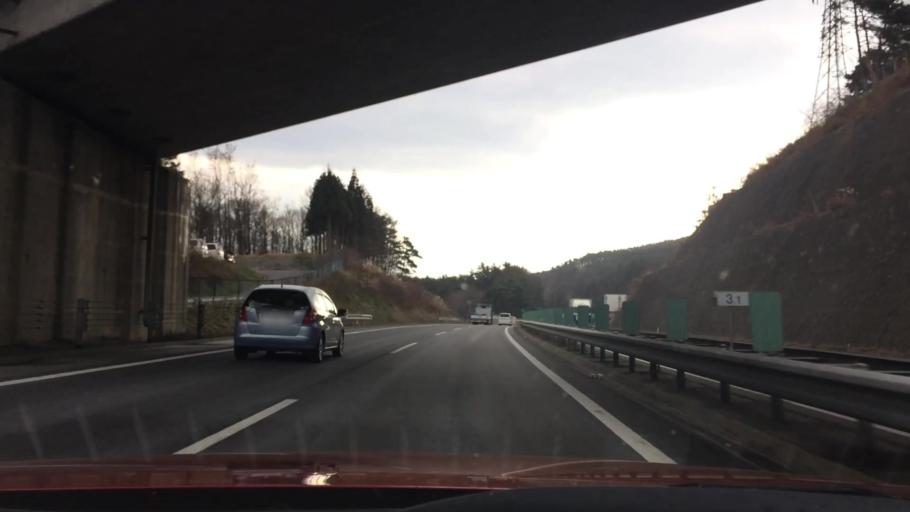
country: JP
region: Nagano
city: Okaya
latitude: 36.0774
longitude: 138.0390
